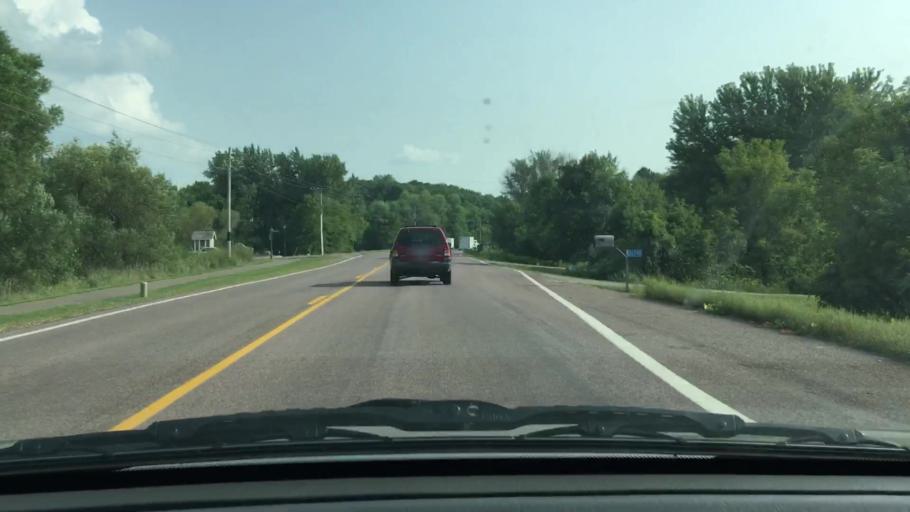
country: US
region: Minnesota
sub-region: Scott County
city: Elko New Market
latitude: 44.5614
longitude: -93.3385
